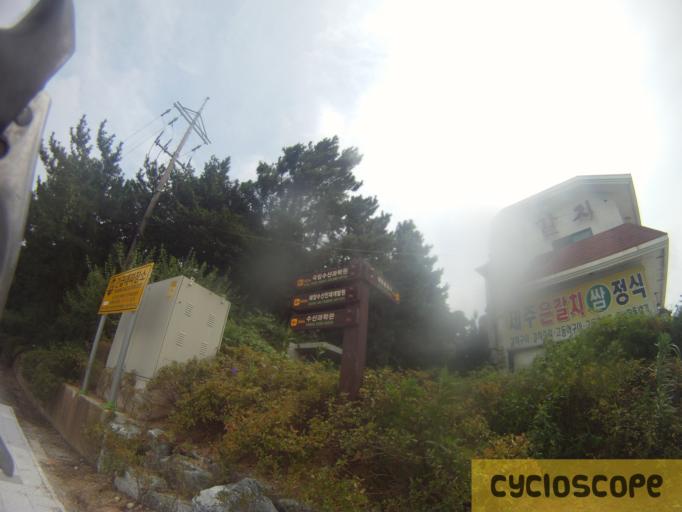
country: KR
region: Busan
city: Kijang
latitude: 35.1937
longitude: 129.2198
